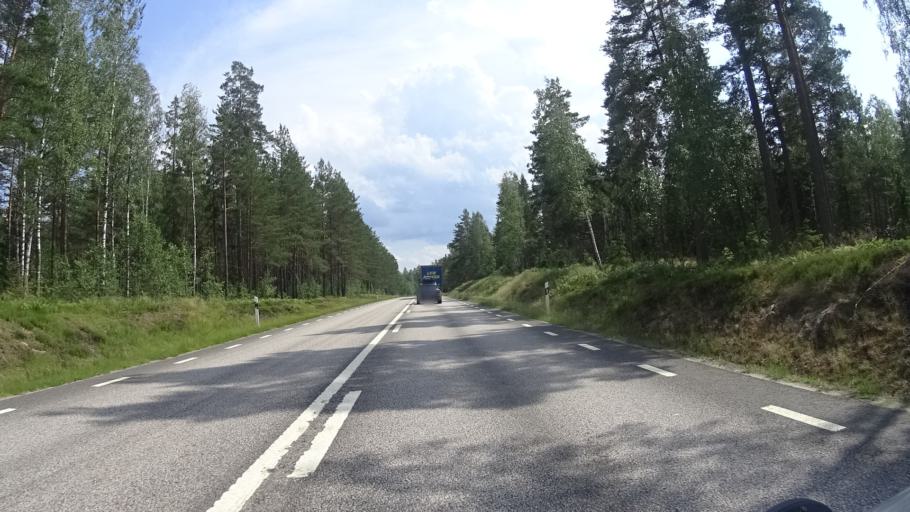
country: SE
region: Kalmar
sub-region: Hultsfreds Kommun
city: Hultsfred
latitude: 57.4787
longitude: 15.8353
